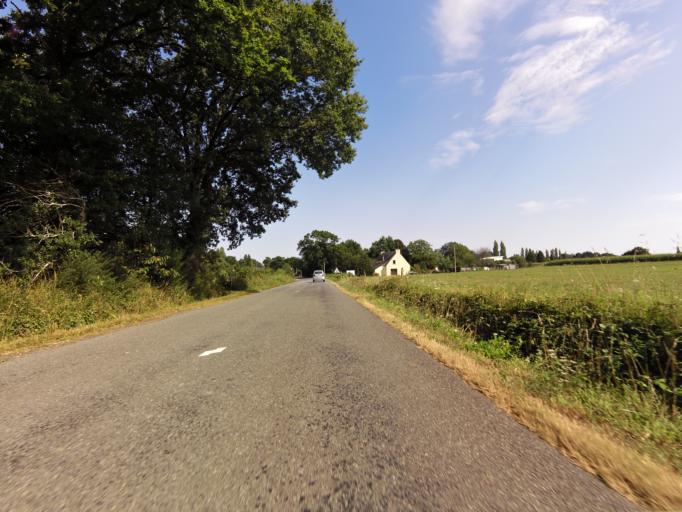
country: FR
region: Brittany
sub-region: Departement du Morbihan
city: Limerzel
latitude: 47.6435
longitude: -2.3655
